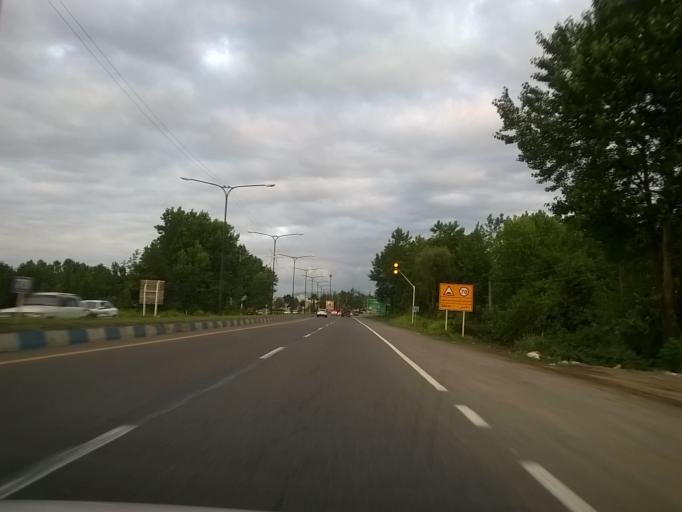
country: IR
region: Gilan
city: Astaneh-ye Ashrafiyeh
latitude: 37.2604
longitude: 49.9283
